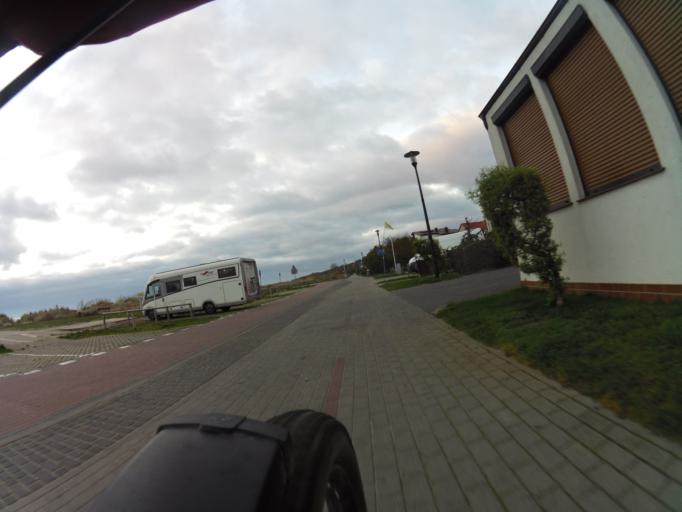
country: PL
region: Pomeranian Voivodeship
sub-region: Powiat pucki
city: Jastarnia
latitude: 54.7342
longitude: 18.5801
